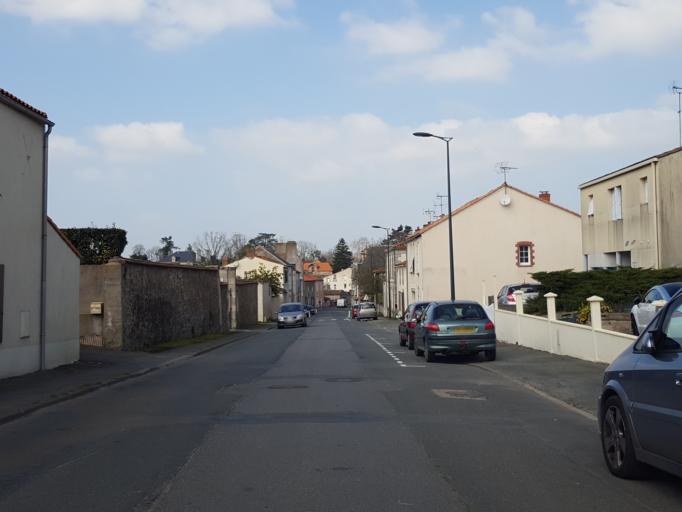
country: FR
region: Pays de la Loire
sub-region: Departement de la Vendee
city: La Chaize-le-Vicomte
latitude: 46.6696
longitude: -1.2892
